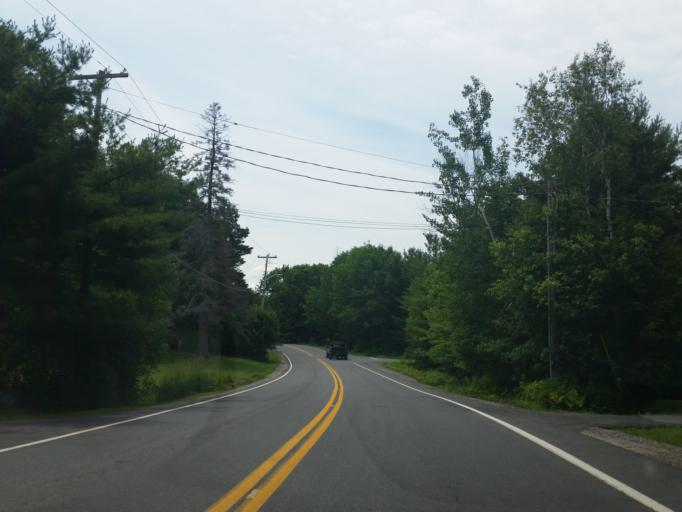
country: CA
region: Ontario
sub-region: Parry Sound District
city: Parry Sound
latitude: 45.3912
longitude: -80.0281
